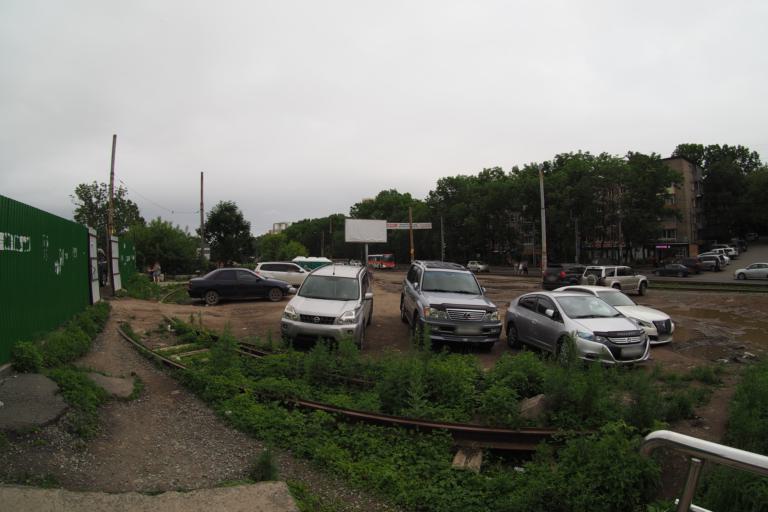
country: RU
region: Primorskiy
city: Vladivostok
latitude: 43.1032
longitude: 131.9401
